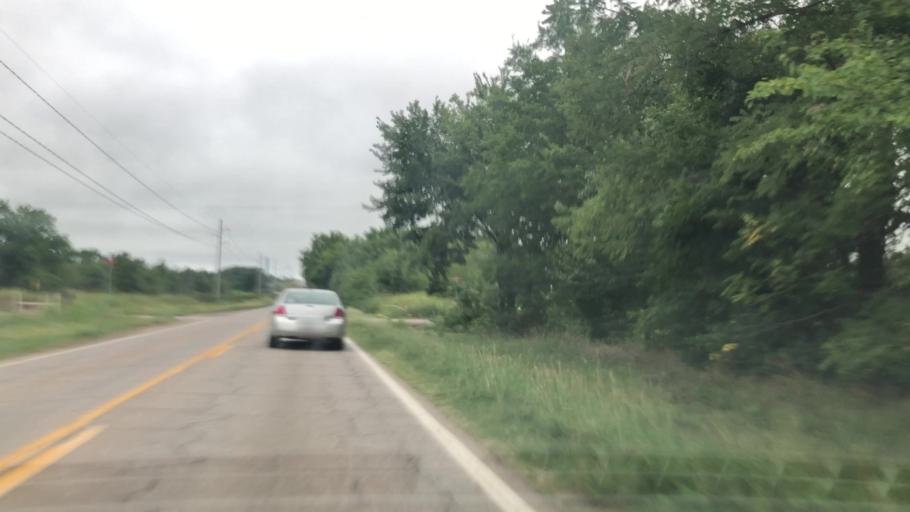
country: US
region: Oklahoma
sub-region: Washington County
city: Dewey
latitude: 36.7280
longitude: -95.8451
